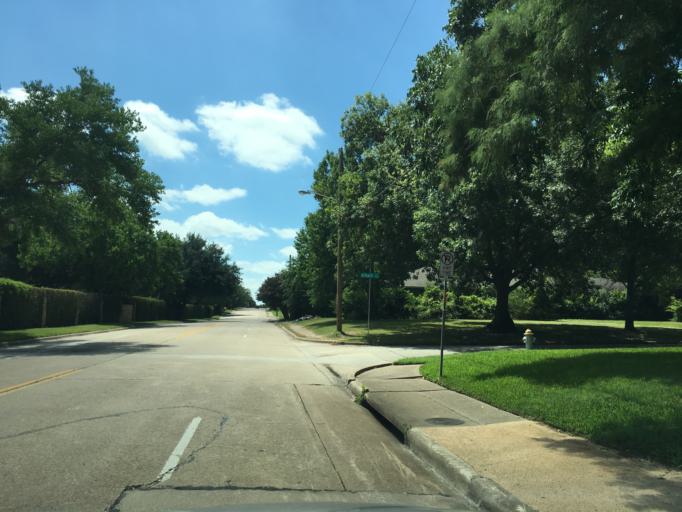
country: US
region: Texas
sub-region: Dallas County
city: Garland
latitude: 32.8415
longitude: -96.6527
